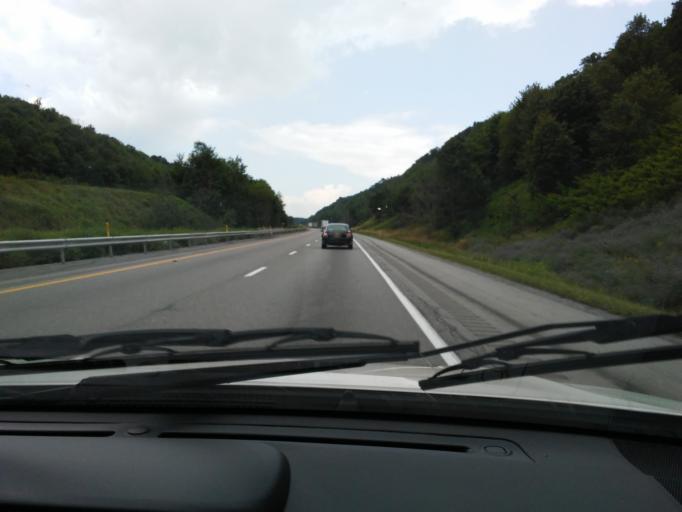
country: US
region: Pennsylvania
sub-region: Centre County
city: Milesburg
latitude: 41.0059
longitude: -77.8667
